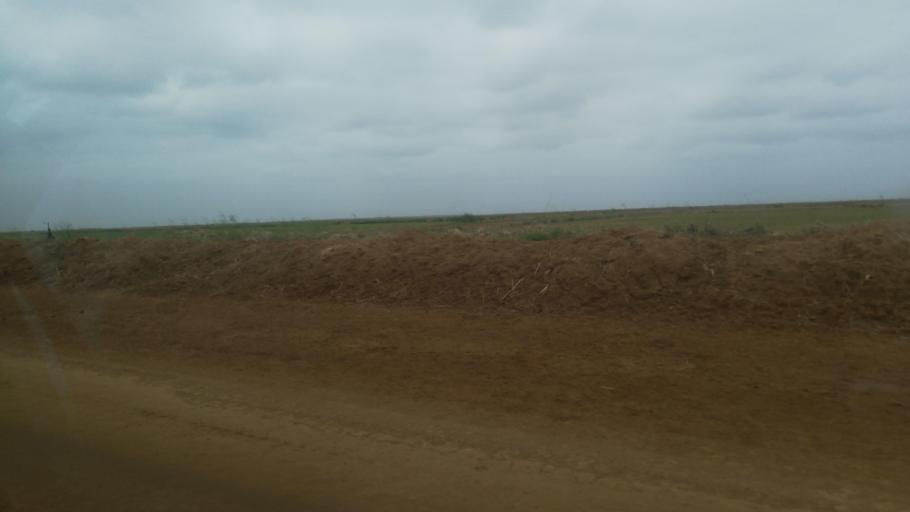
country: SN
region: Saint-Louis
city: Saint-Louis
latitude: 16.3184
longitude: -16.2358
